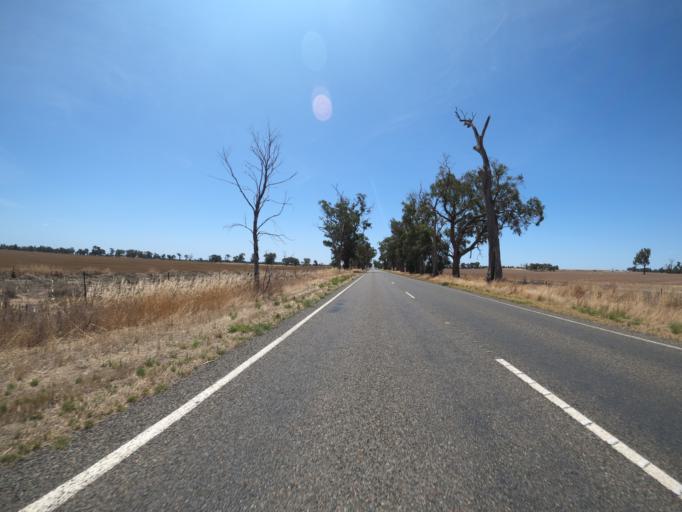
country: AU
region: Victoria
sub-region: Moira
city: Yarrawonga
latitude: -36.0614
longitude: 145.9955
